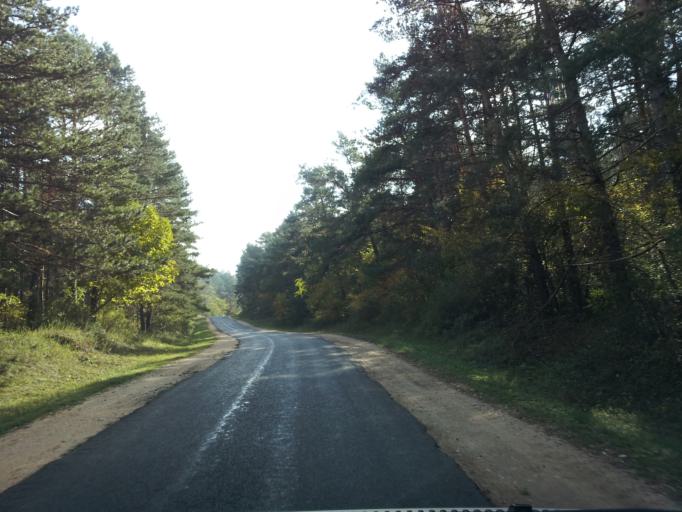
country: HU
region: Gyor-Moson-Sopron
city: Bakonyszentlaszlo
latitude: 47.3748
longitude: 17.8120
